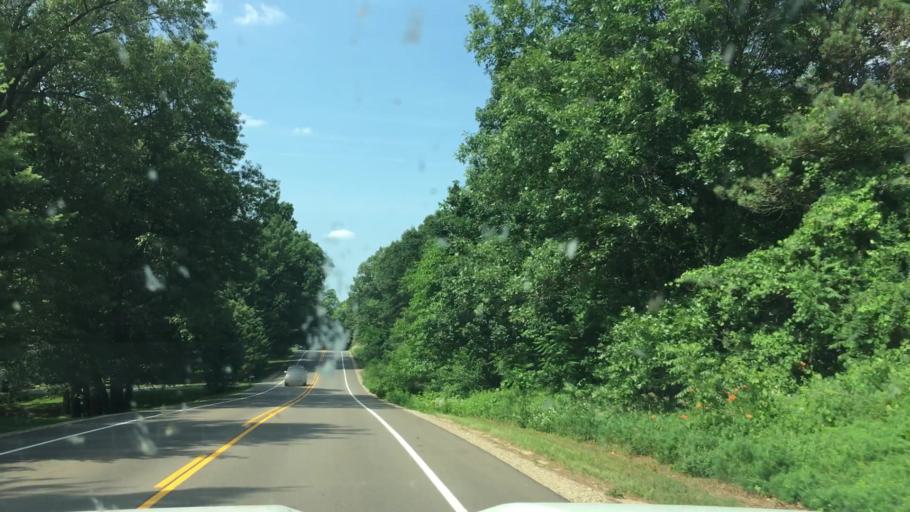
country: US
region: Michigan
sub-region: Allegan County
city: Plainwell
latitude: 42.4484
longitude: -85.6025
